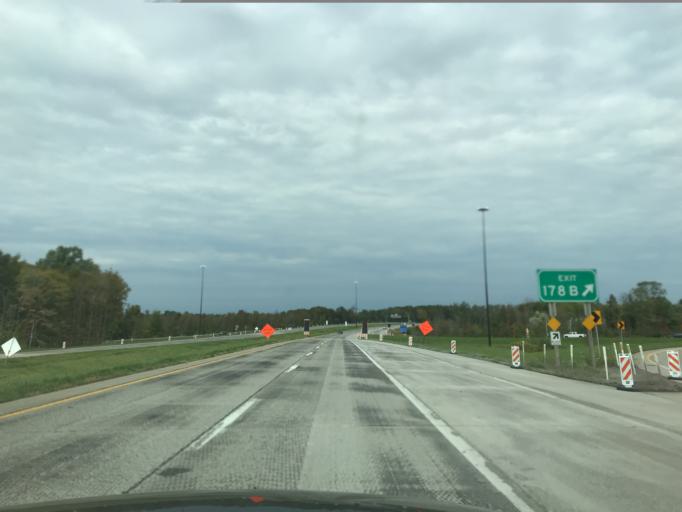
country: US
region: Pennsylvania
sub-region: Erie County
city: Erie
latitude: 42.0332
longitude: -80.1223
